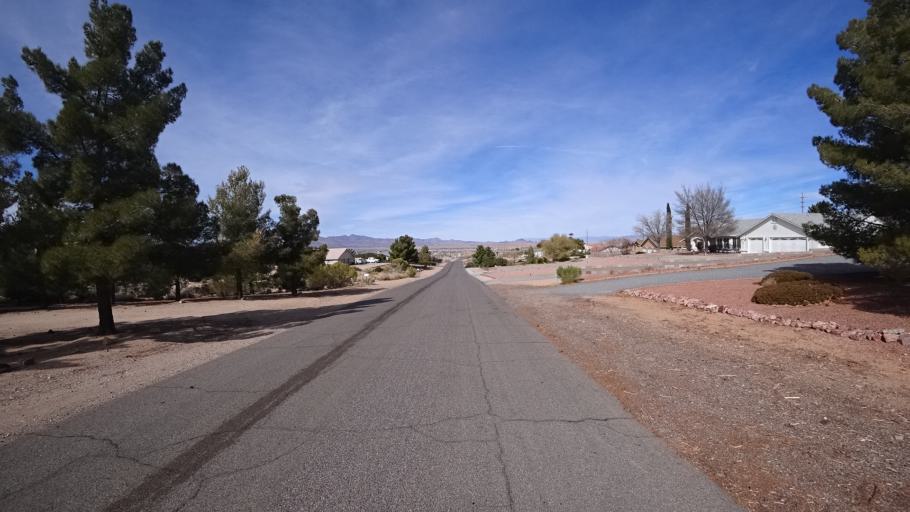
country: US
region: Arizona
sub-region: Mohave County
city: Kingman
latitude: 35.1921
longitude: -113.9874
